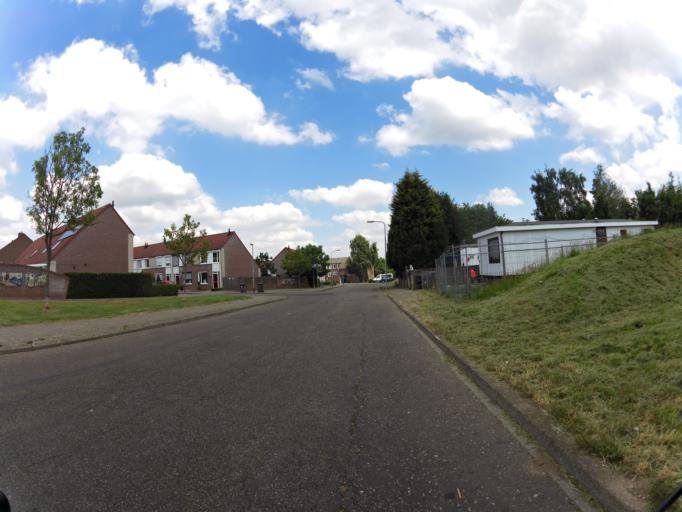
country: NL
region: Limburg
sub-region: Gemeente Kerkrade
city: Kerkrade
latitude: 50.8754
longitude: 6.0722
